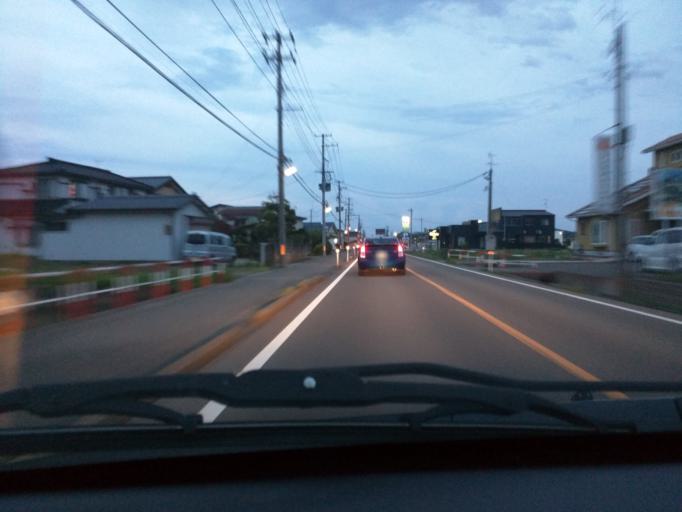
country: JP
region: Niigata
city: Kashiwazaki
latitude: 37.3486
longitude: 138.6077
